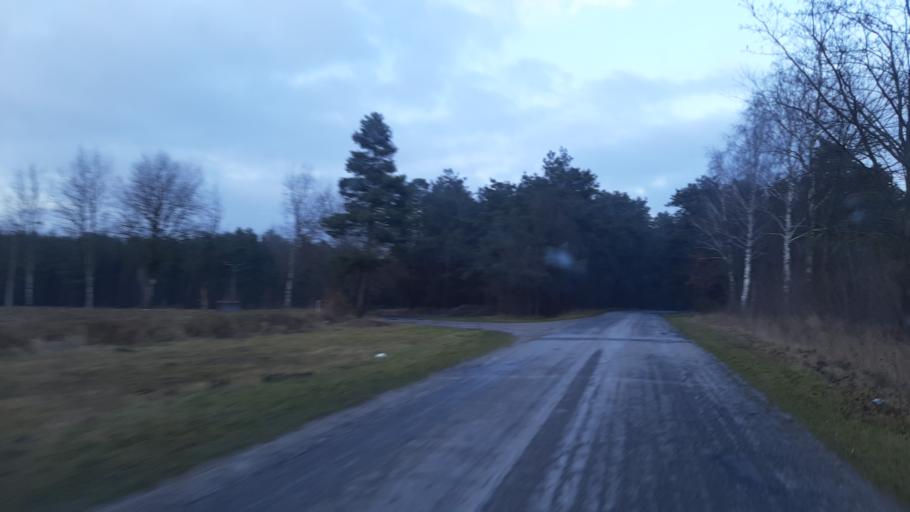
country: PL
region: Lublin Voivodeship
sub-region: Powiat lubartowski
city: Kamionka
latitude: 51.4786
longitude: 22.4693
